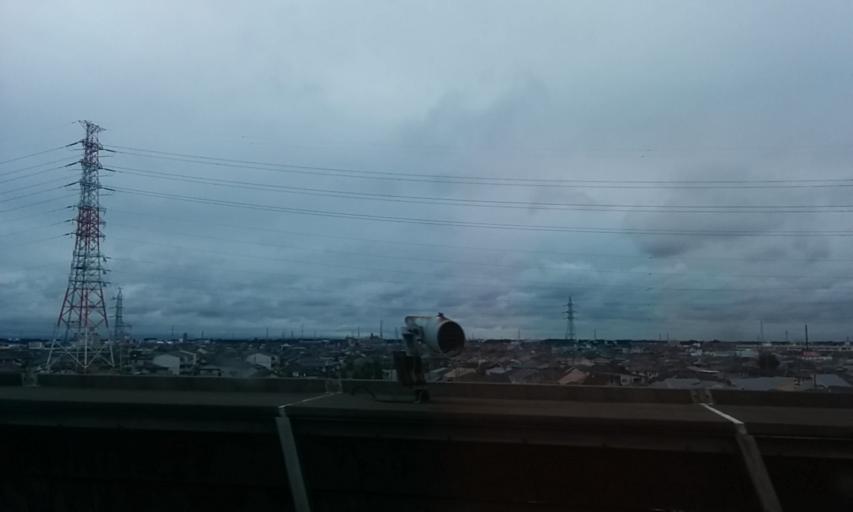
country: JP
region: Tochigi
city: Oyama
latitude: 36.2992
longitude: 139.7965
